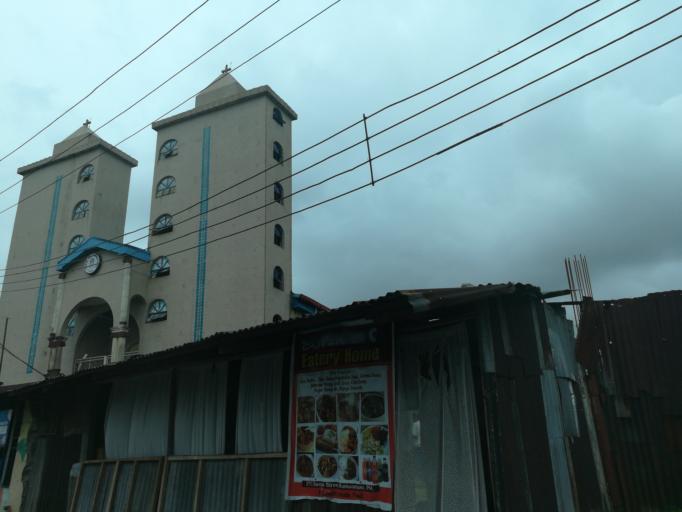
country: NG
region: Rivers
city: Port Harcourt
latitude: 4.8296
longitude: 7.0263
